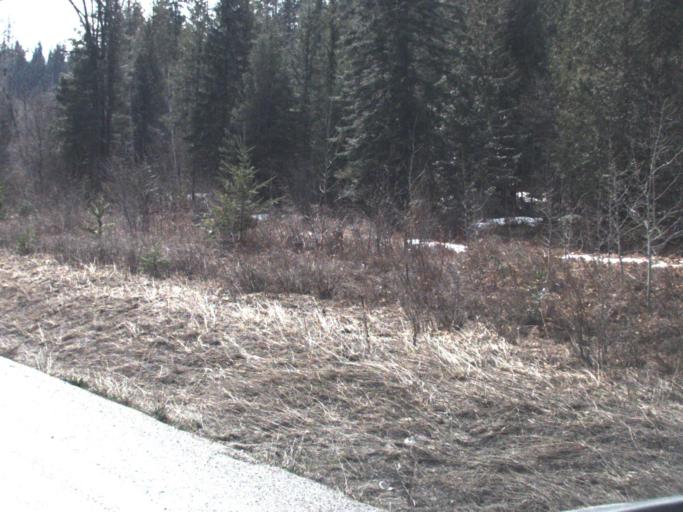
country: US
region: Washington
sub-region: Stevens County
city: Chewelah
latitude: 48.5526
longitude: -117.3415
